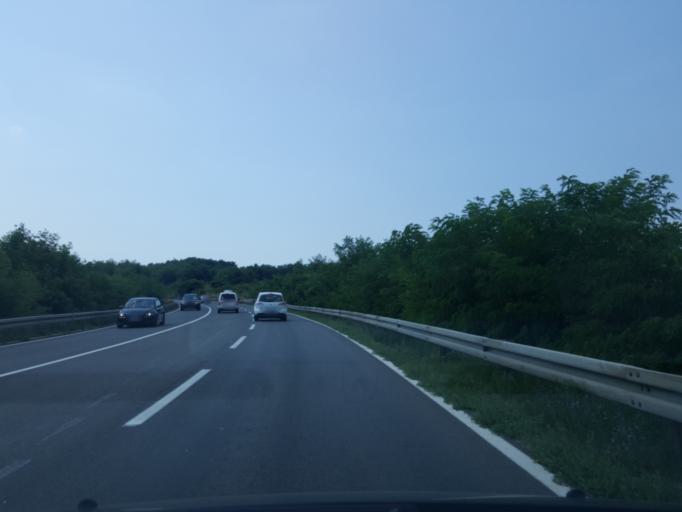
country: RS
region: Central Serbia
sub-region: Belgrade
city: Sopot
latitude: 44.5457
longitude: 20.6587
